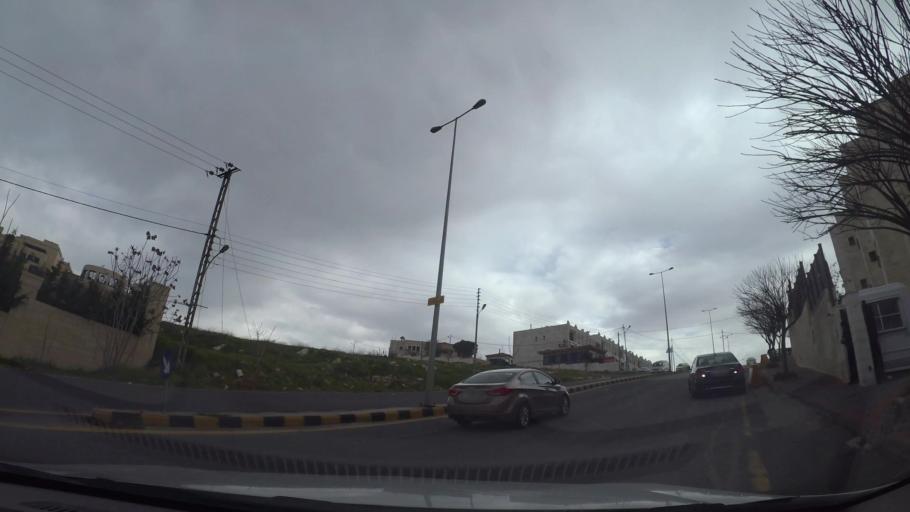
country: JO
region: Amman
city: Wadi as Sir
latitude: 31.9917
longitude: 35.8128
